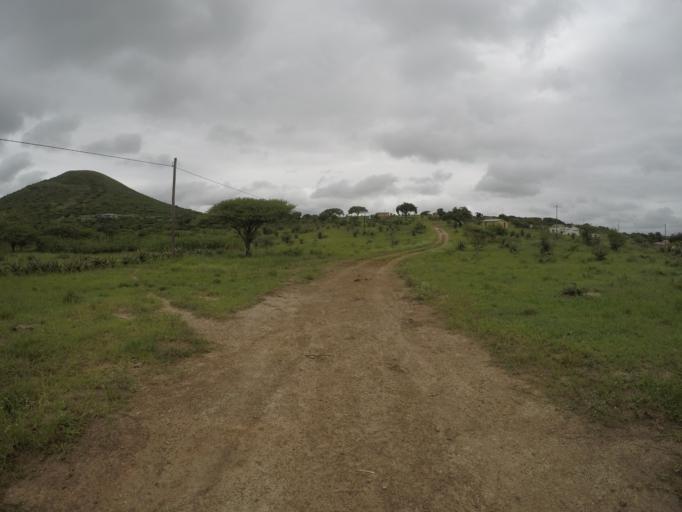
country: ZA
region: KwaZulu-Natal
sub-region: uThungulu District Municipality
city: Empangeni
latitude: -28.5975
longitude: 31.8499
